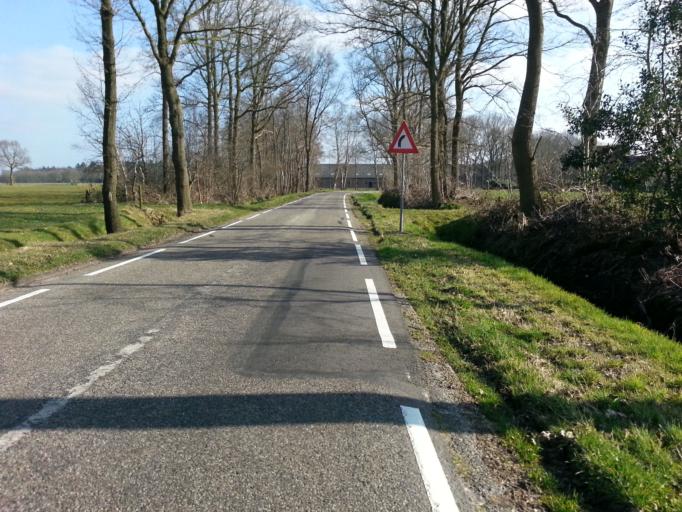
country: NL
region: Utrecht
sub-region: Gemeente Leusden
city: Leusden
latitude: 52.0967
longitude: 5.4741
